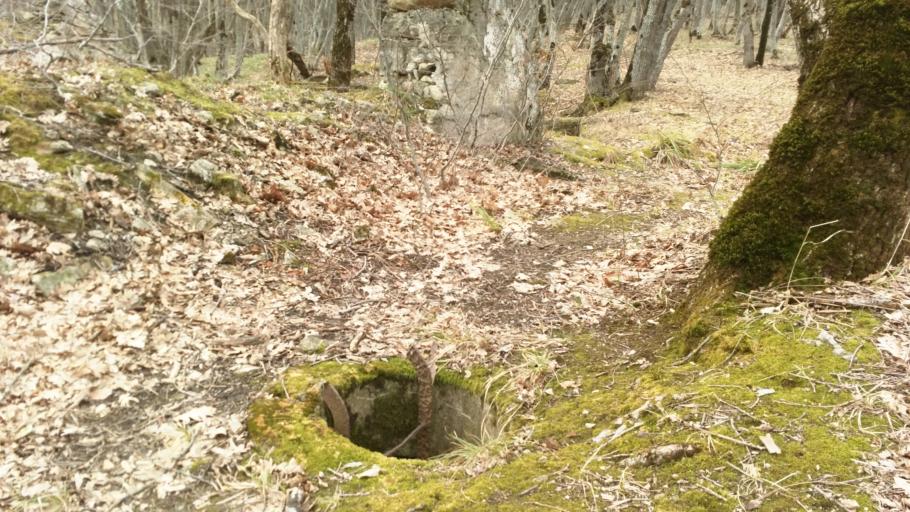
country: RU
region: Stavropol'skiy
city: Zheleznovodsk
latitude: 44.1271
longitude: 43.0224
